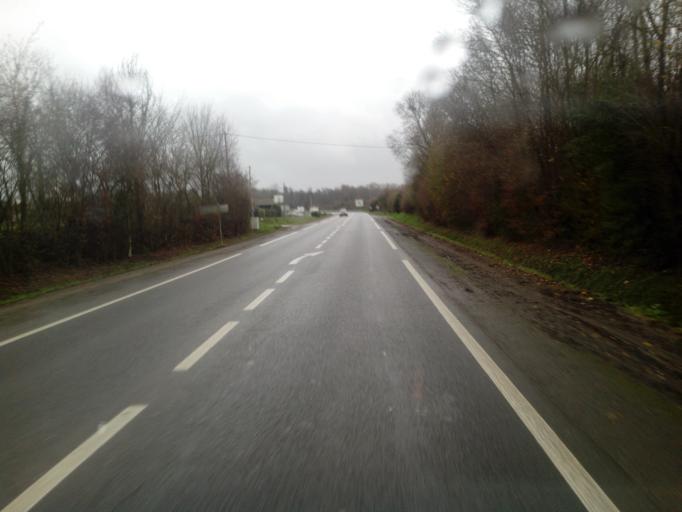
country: FR
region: Brittany
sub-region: Departement d'Ille-et-Vilaine
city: Betton
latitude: 48.1554
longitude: -1.6310
